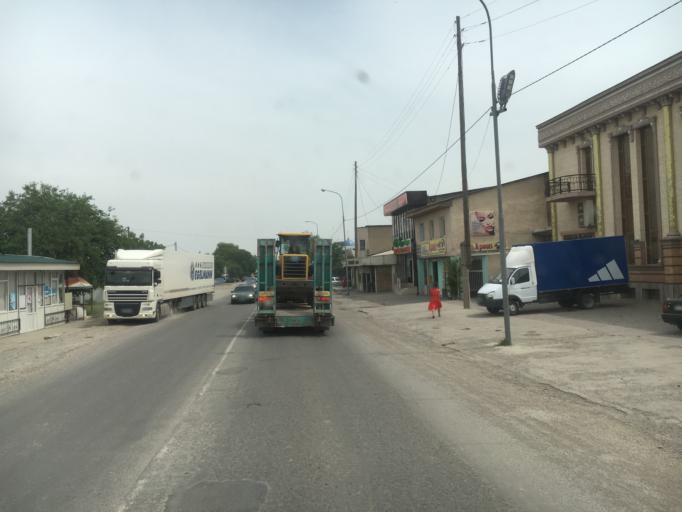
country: KZ
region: Ongtustik Qazaqstan
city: Shymkent
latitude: 42.3425
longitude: 69.5235
